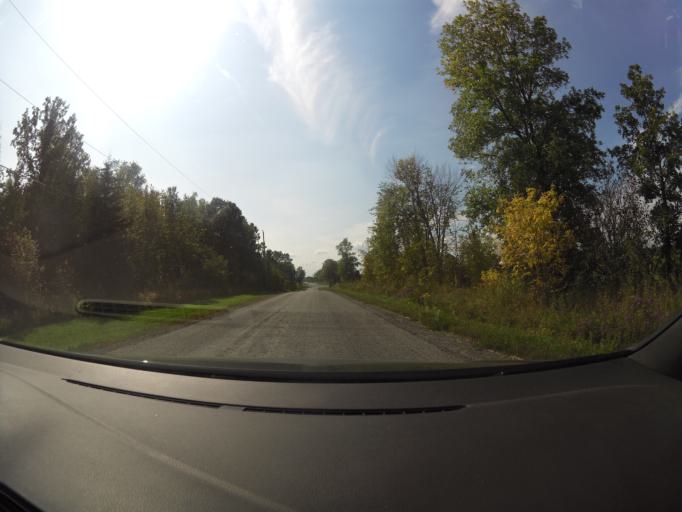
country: CA
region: Ontario
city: Carleton Place
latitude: 45.2872
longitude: -76.2366
